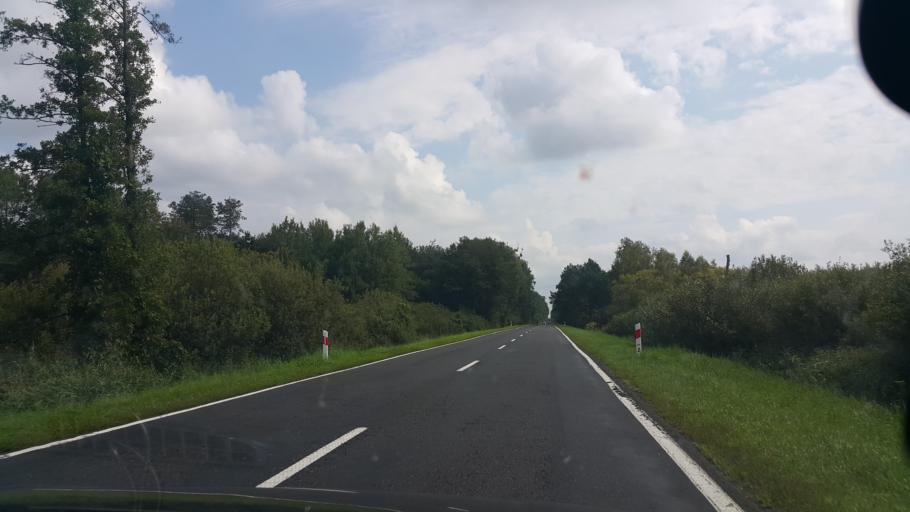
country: PL
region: Lublin Voivodeship
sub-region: Powiat wlodawski
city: Hansk
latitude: 51.4872
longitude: 23.3493
